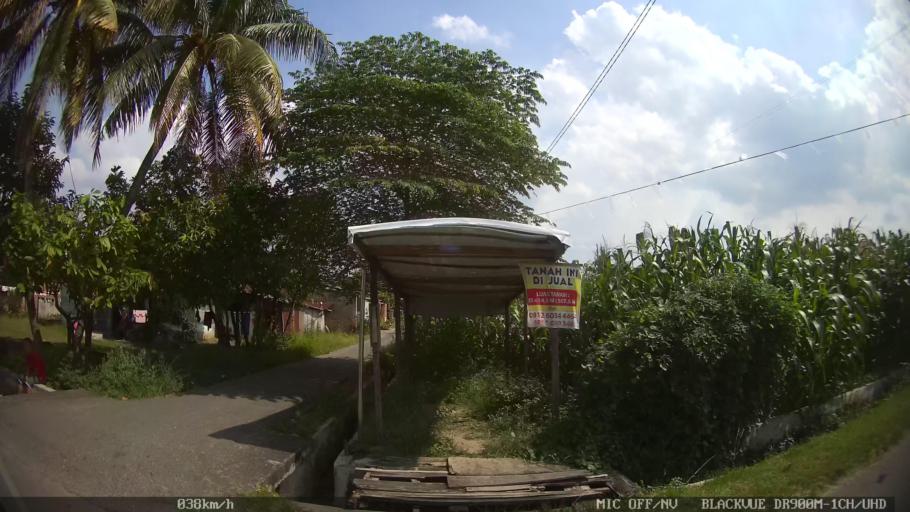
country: ID
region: North Sumatra
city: Binjai
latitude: 3.6133
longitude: 98.5318
